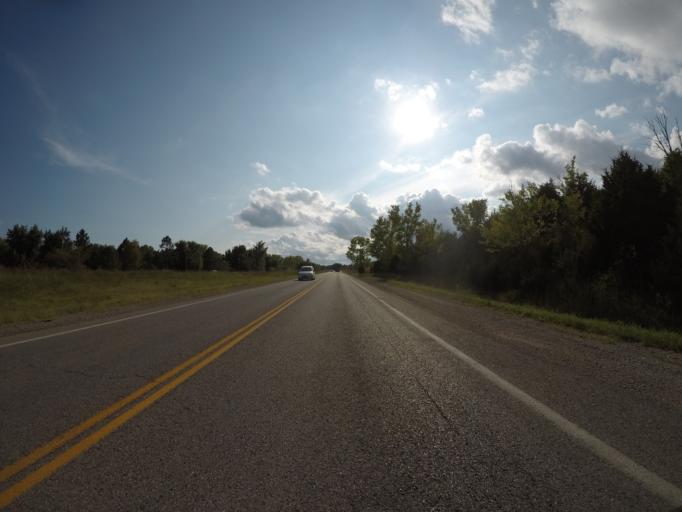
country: US
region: Kansas
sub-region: Jefferson County
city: Valley Falls
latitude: 39.1929
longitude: -95.5527
